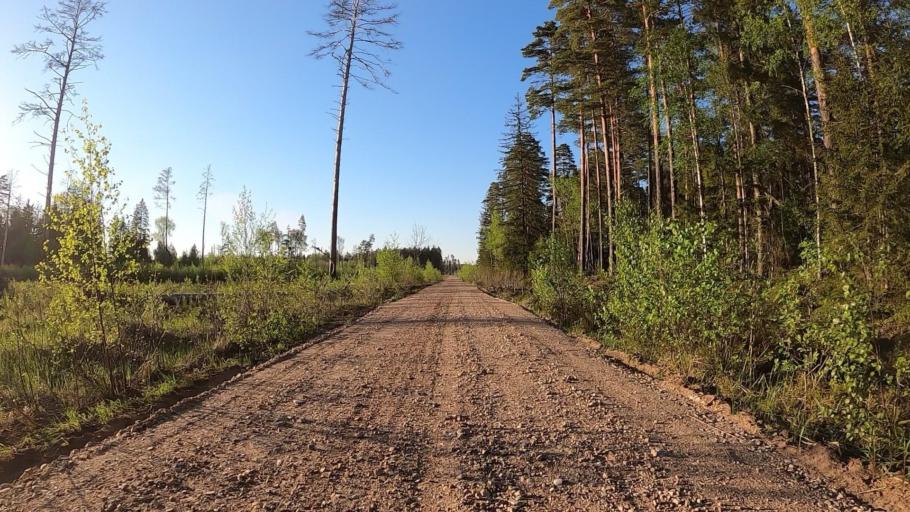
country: LV
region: Kekava
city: Kekava
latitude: 56.7688
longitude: 24.2227
